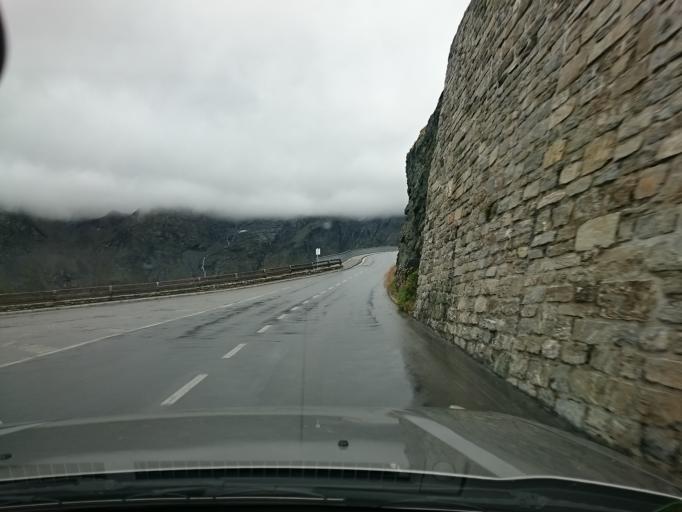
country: AT
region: Carinthia
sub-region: Politischer Bezirk Spittal an der Drau
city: Heiligenblut
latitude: 47.0730
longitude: 12.7584
